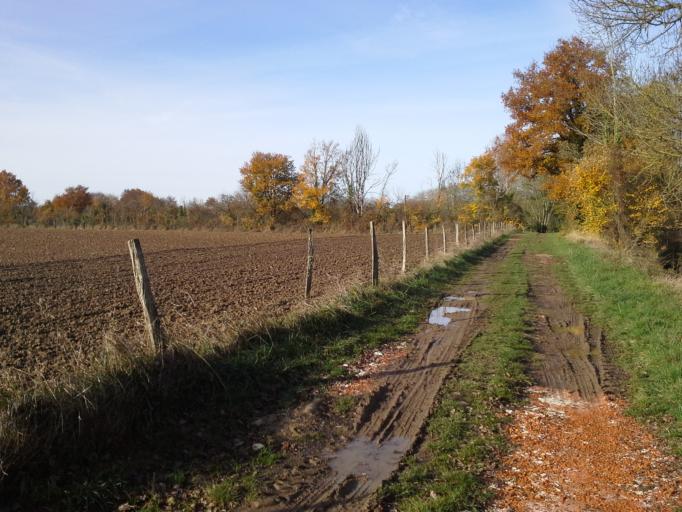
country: FR
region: Poitou-Charentes
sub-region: Departement de la Vienne
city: Pleumartin
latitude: 46.6398
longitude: 0.7521
